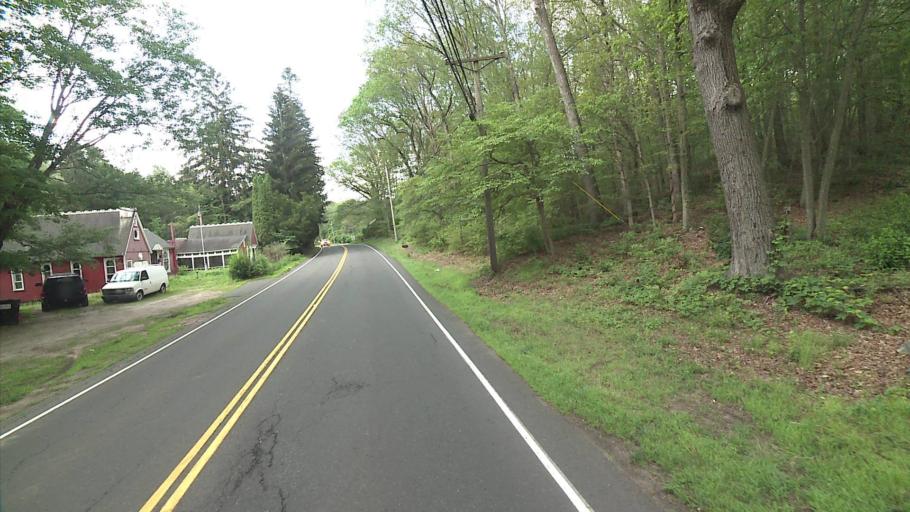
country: US
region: Connecticut
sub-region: Middlesex County
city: Higganum
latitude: 41.4533
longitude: -72.5551
